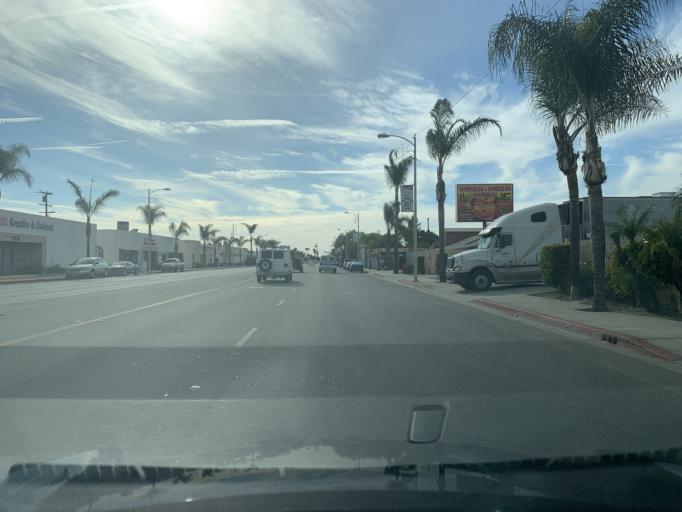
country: US
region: California
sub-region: Los Angeles County
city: South El Monte
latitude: 34.0460
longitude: -118.0440
